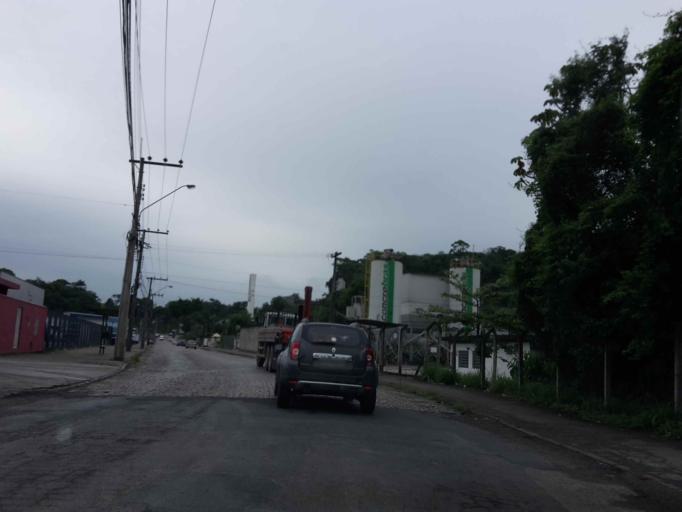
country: BR
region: Santa Catarina
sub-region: Blumenau
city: Blumenau
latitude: -26.8614
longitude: -49.0995
